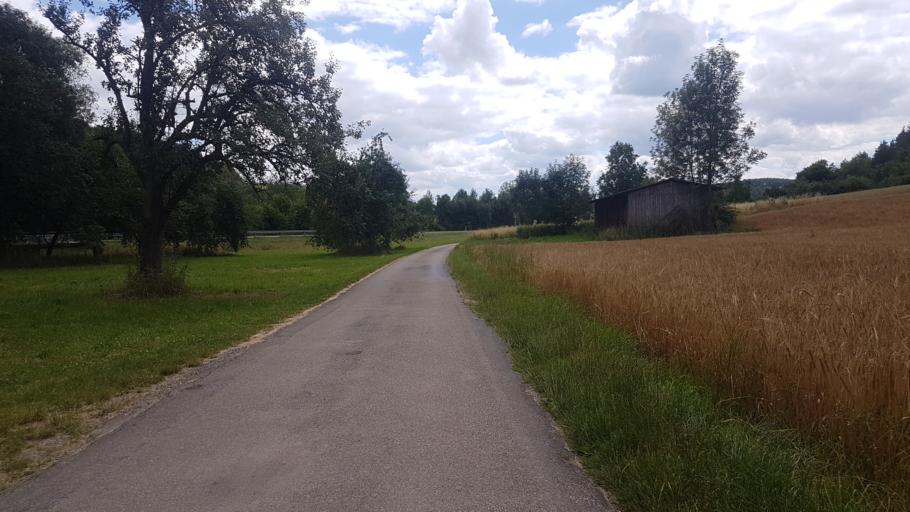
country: DE
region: Baden-Wuerttemberg
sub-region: Regierungsbezirk Stuttgart
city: Bad Mergentheim
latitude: 49.4719
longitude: 9.7728
